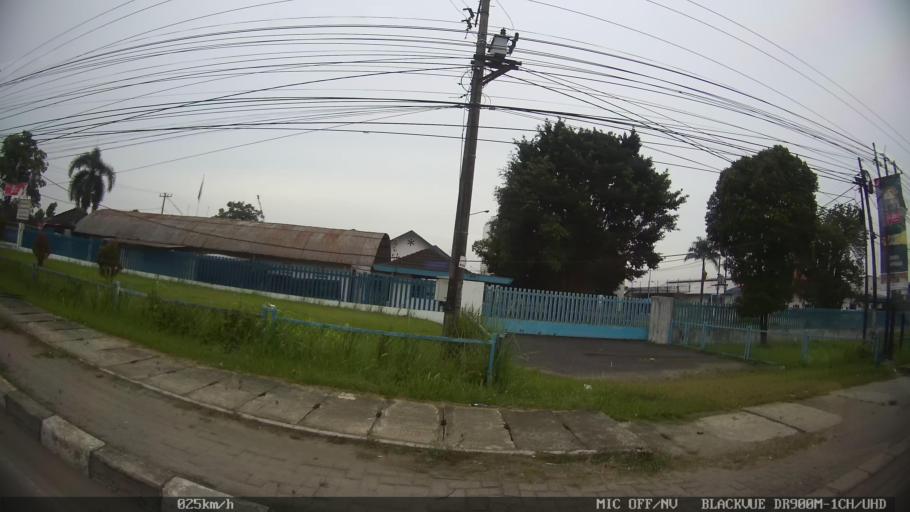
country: ID
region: North Sumatra
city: Deli Tua
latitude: 3.5323
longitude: 98.7314
